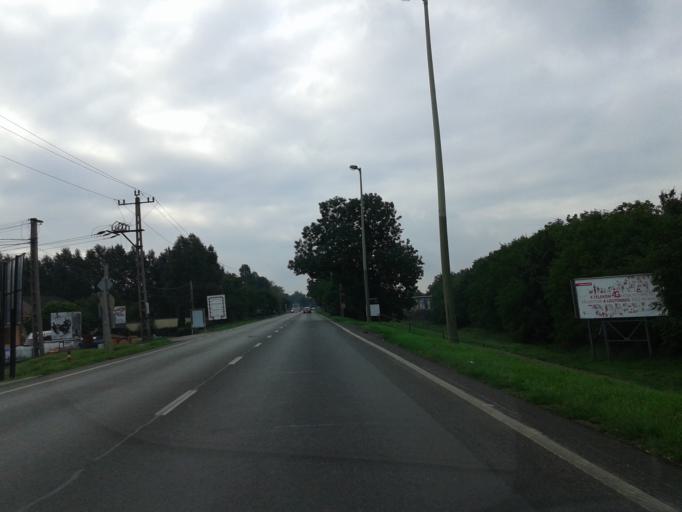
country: HU
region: Csongrad
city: Szeged
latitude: 46.2382
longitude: 20.1684
